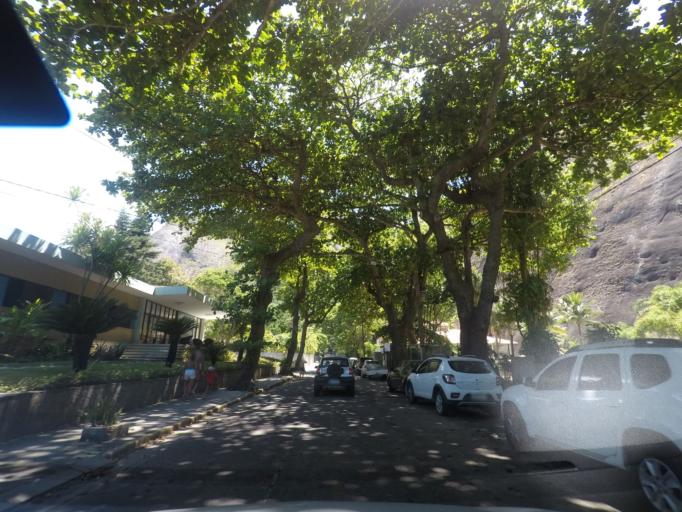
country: BR
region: Rio de Janeiro
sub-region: Niteroi
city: Niteroi
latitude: -22.9750
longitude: -43.0296
